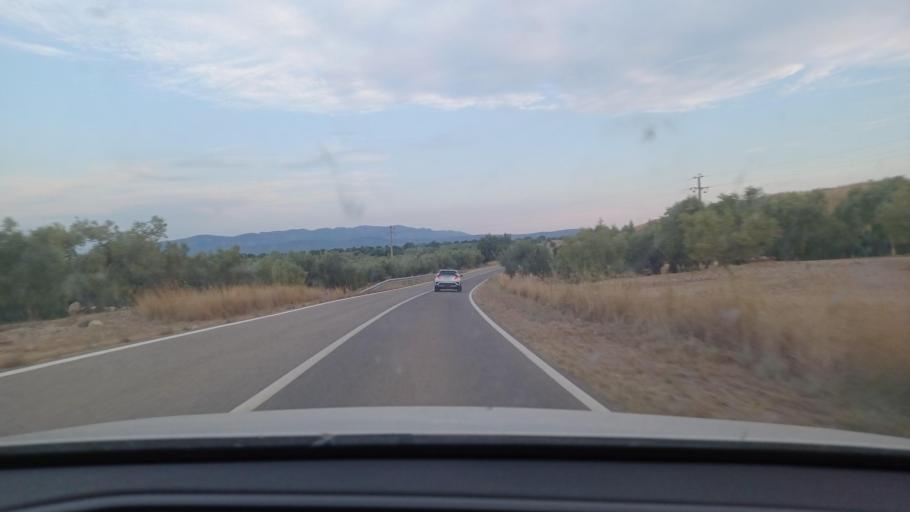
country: ES
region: Catalonia
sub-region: Provincia de Tarragona
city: Mas de Barberans
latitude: 40.7174
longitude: 0.4013
